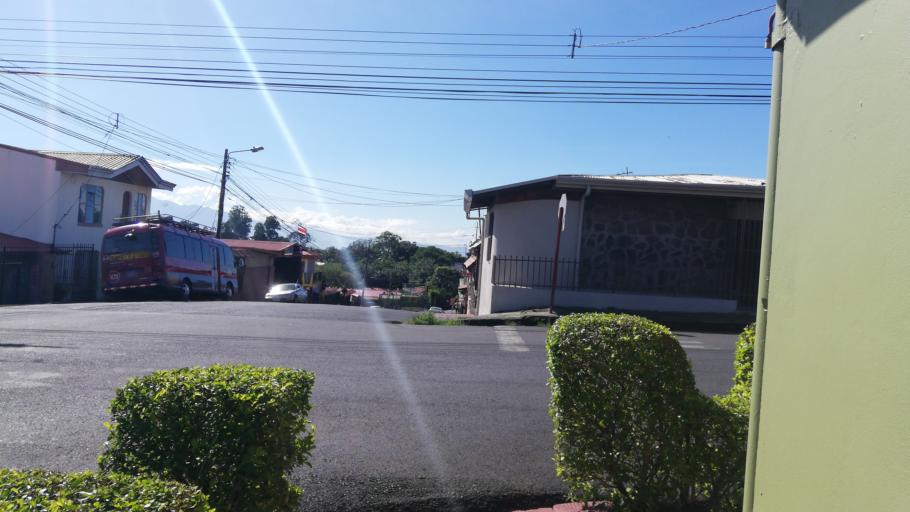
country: CR
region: Alajuela
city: San Juan
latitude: 10.0712
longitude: -84.3091
